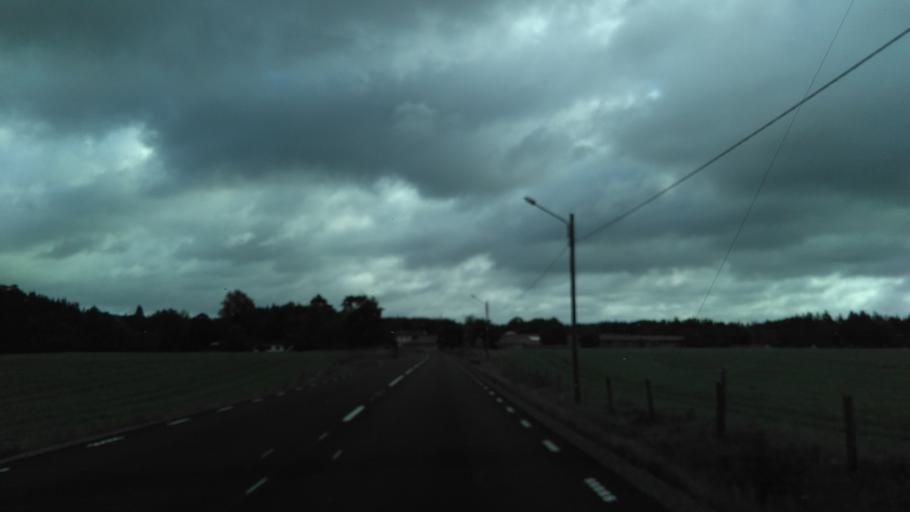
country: SE
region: Vaestra Goetaland
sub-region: Marks Kommun
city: Fritsla
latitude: 57.5873
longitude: 12.7456
